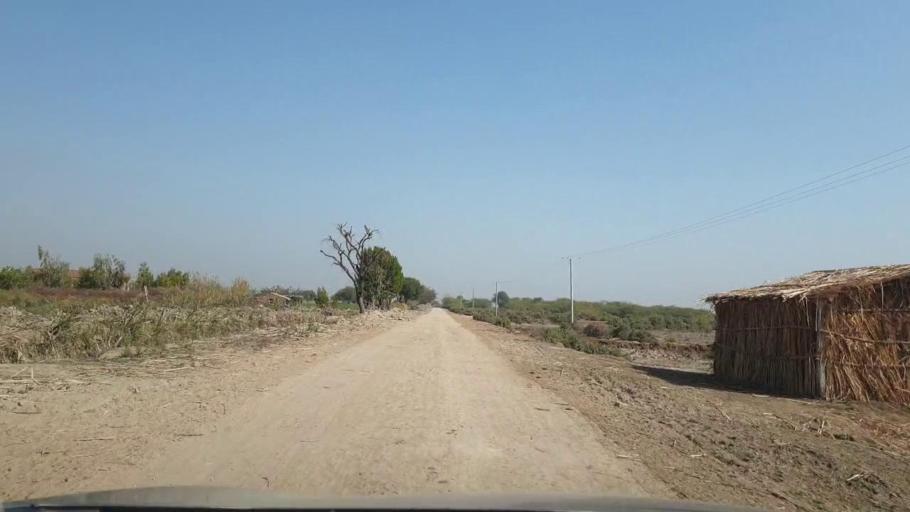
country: PK
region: Sindh
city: Berani
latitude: 25.6648
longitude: 68.8888
